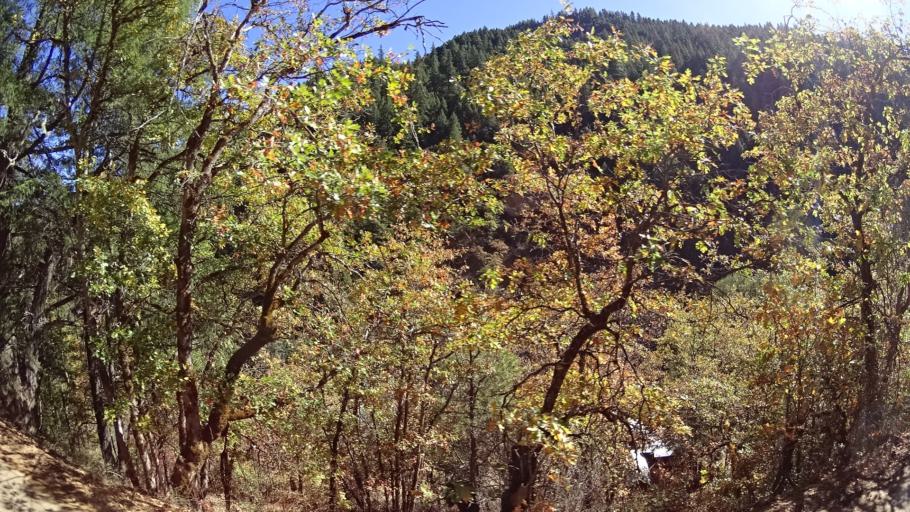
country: US
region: California
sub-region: Siskiyou County
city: Happy Camp
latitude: 41.2945
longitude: -123.1114
